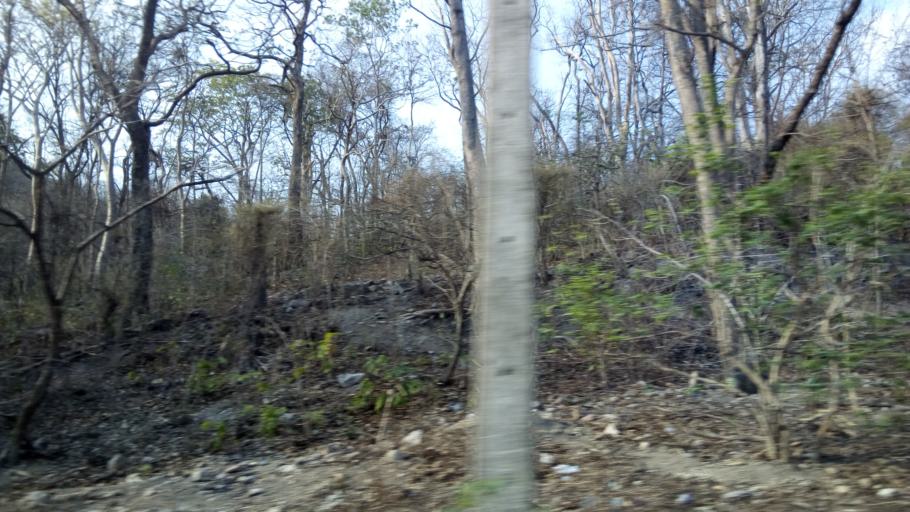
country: TH
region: Sara Buri
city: Saraburi
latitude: 14.4588
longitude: 100.9503
